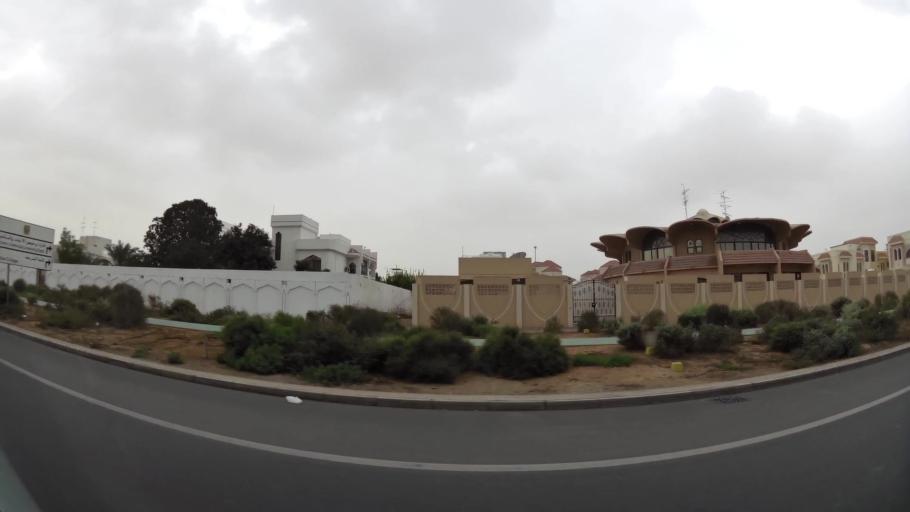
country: AE
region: Abu Dhabi
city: Abu Dhabi
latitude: 24.4460
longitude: 54.4150
